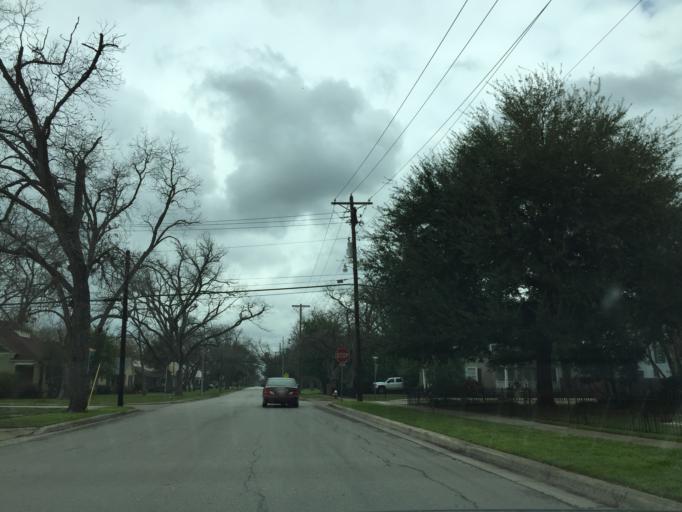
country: US
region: Texas
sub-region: Bastrop County
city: Bastrop
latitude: 30.1123
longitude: -97.3176
